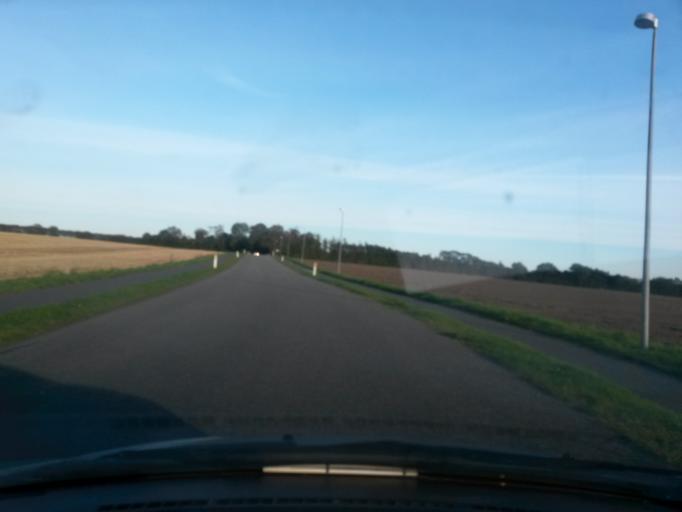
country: DK
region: Central Jutland
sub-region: Silkeborg Kommune
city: Kjellerup
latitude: 56.3321
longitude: 9.4277
